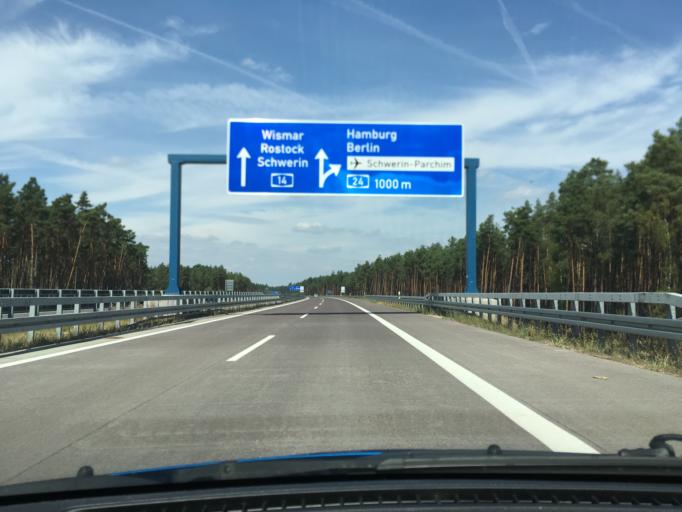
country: DE
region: Mecklenburg-Vorpommern
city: Gross Laasch
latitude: 53.4076
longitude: 11.5301
